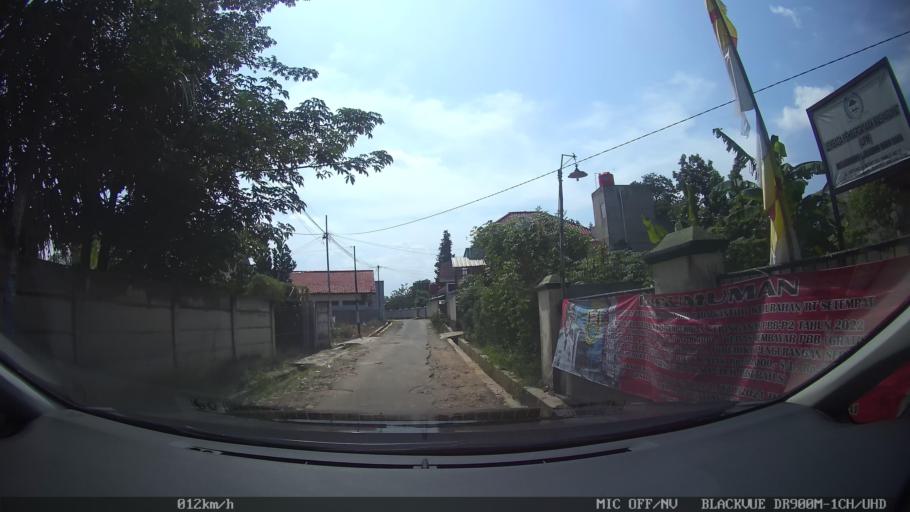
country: ID
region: Lampung
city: Kedaton
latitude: -5.3706
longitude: 105.2534
